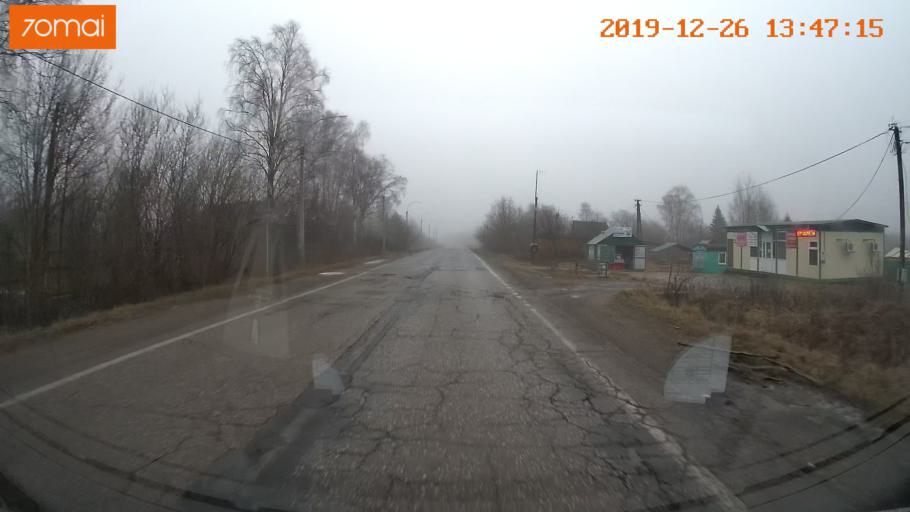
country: RU
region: Vologda
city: Sheksna
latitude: 58.6861
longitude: 38.5324
